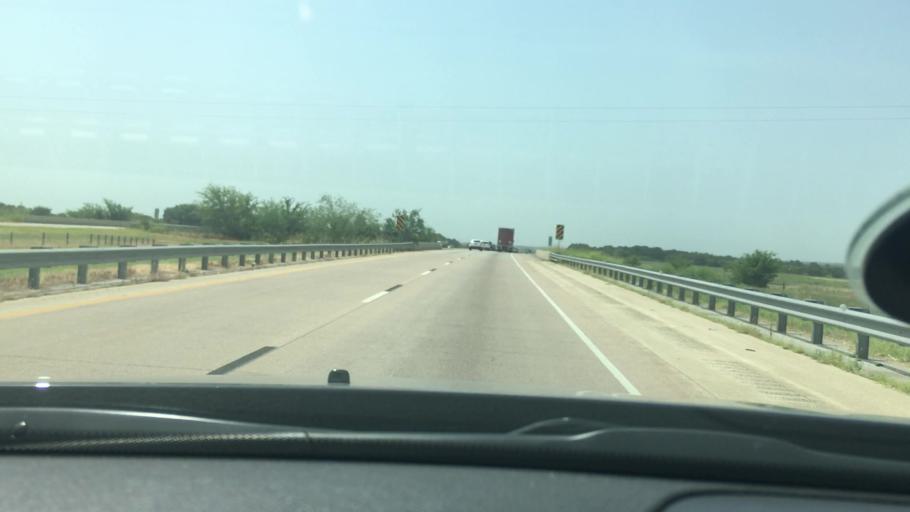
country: US
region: Oklahoma
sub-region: Garvin County
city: Pauls Valley
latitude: 34.6819
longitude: -97.2285
